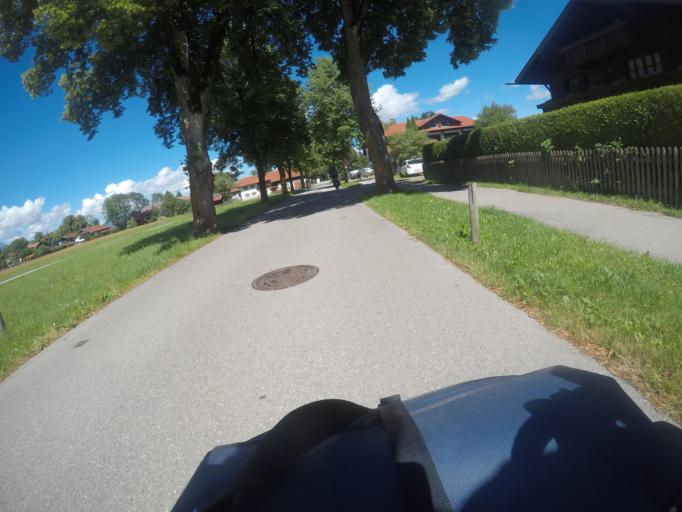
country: DE
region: Bavaria
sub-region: Swabia
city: Schwangau
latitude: 47.5837
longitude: 10.7297
